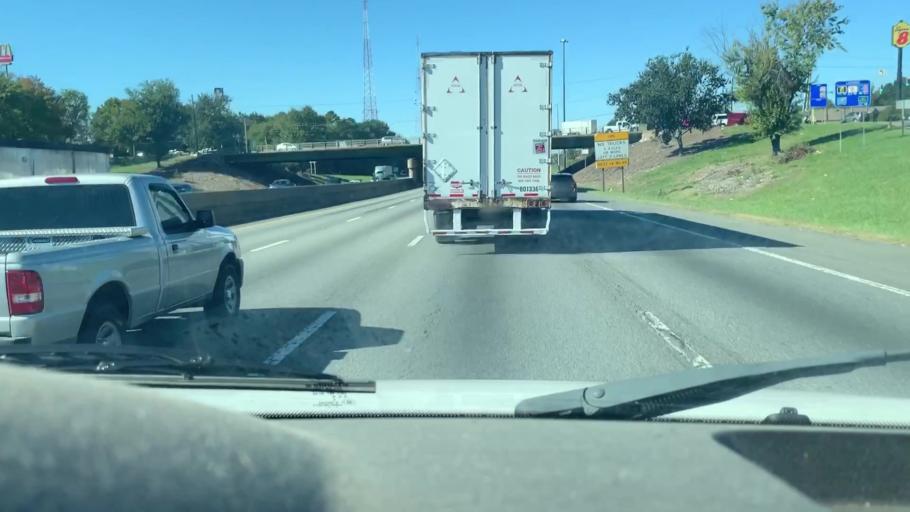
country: US
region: North Carolina
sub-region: Mecklenburg County
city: Charlotte
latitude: 35.2786
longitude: -80.7924
